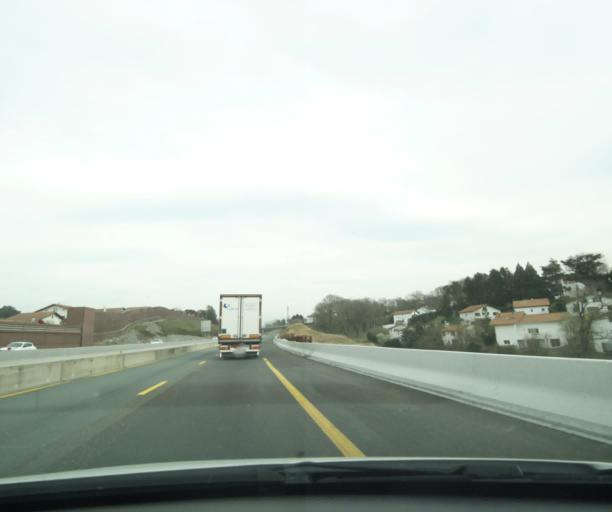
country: FR
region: Aquitaine
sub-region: Departement des Pyrenees-Atlantiques
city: Saint-Jean-de-Luz
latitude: 43.3746
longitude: -1.6630
